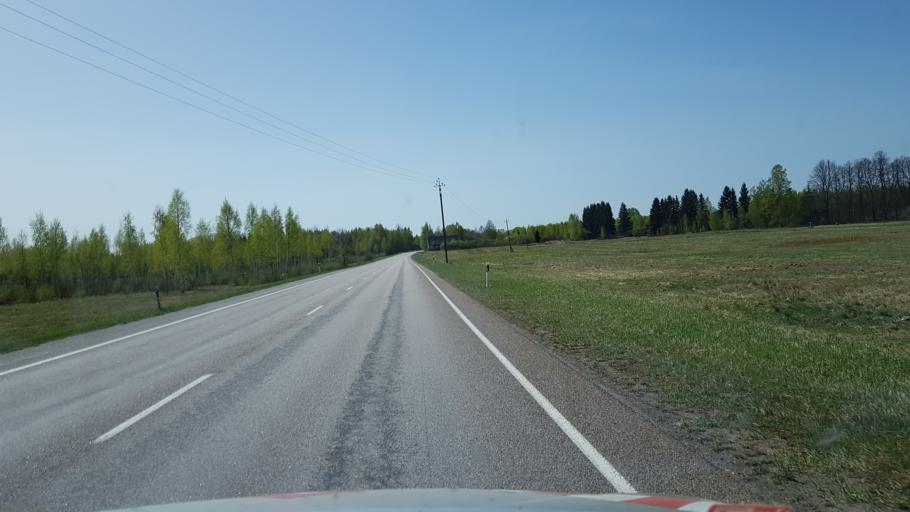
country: EE
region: Valgamaa
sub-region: Valga linn
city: Valga
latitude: 57.8120
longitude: 26.0418
